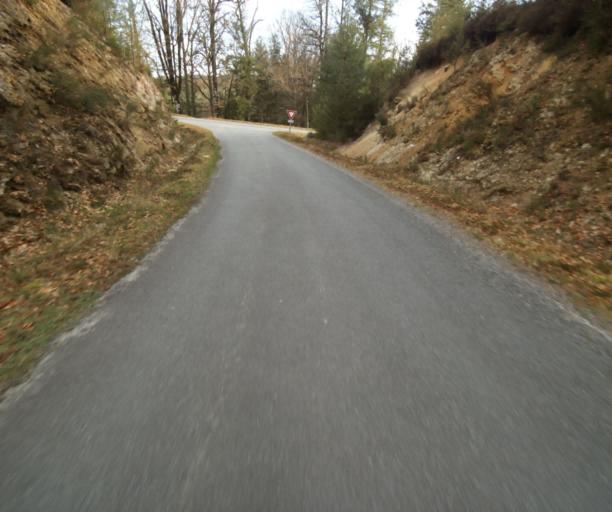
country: FR
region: Limousin
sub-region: Departement de la Correze
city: Correze
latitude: 45.4113
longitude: 1.9166
